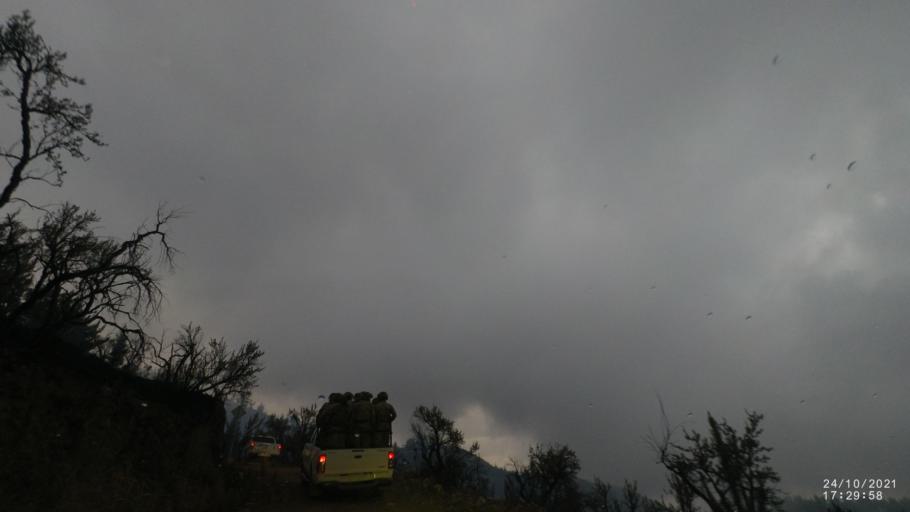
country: BO
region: Cochabamba
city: Cochabamba
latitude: -17.3231
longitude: -66.1315
